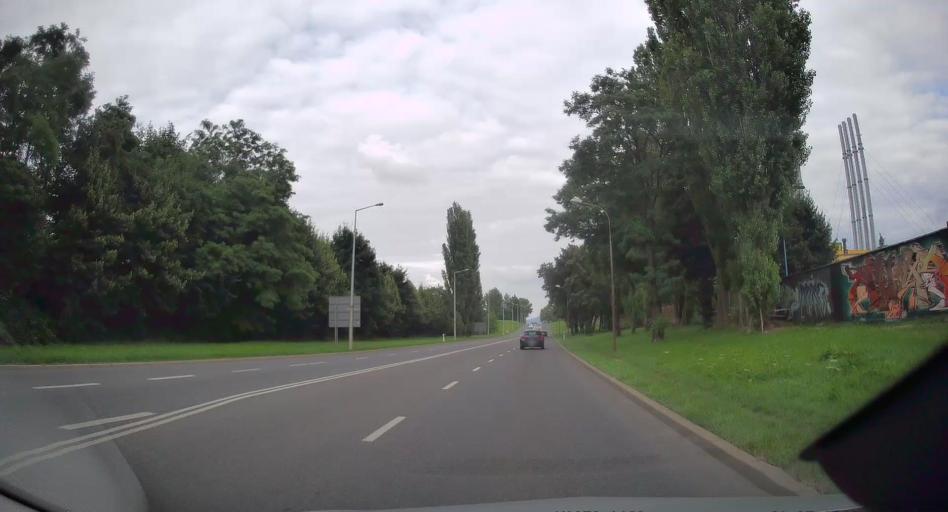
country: PL
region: Lower Silesian Voivodeship
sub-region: Powiat swidnicki
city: Swidnica
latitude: 50.8528
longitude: 16.4888
